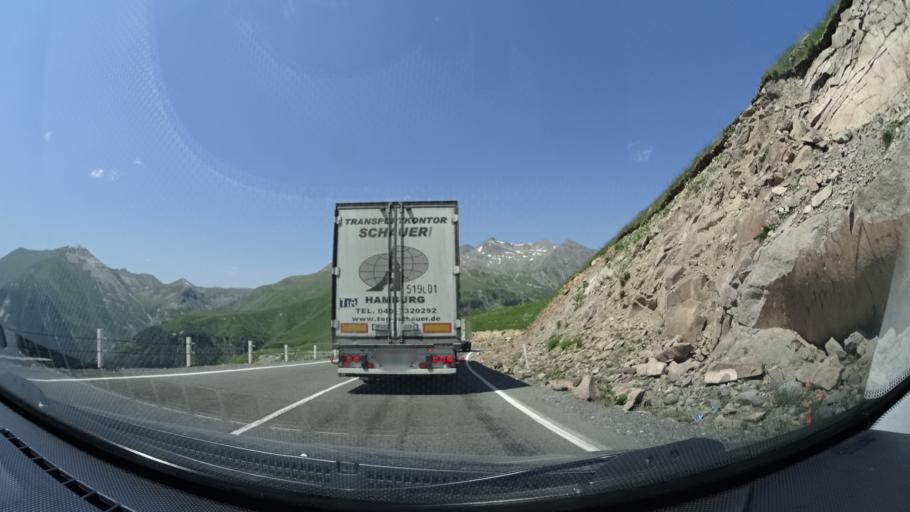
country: GE
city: Gudauri
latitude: 42.4996
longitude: 44.4513
